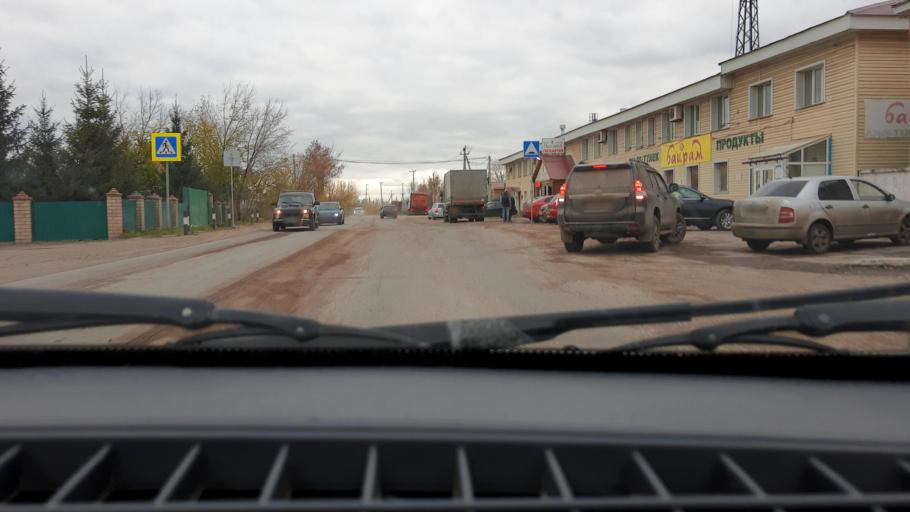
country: RU
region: Bashkortostan
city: Ufa
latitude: 54.5692
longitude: 55.9315
